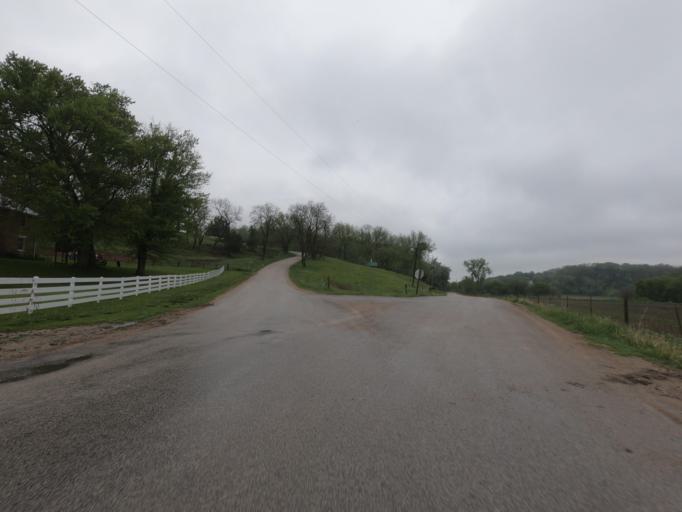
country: US
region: Wisconsin
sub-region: Grant County
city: Hazel Green
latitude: 42.4807
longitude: -90.4878
